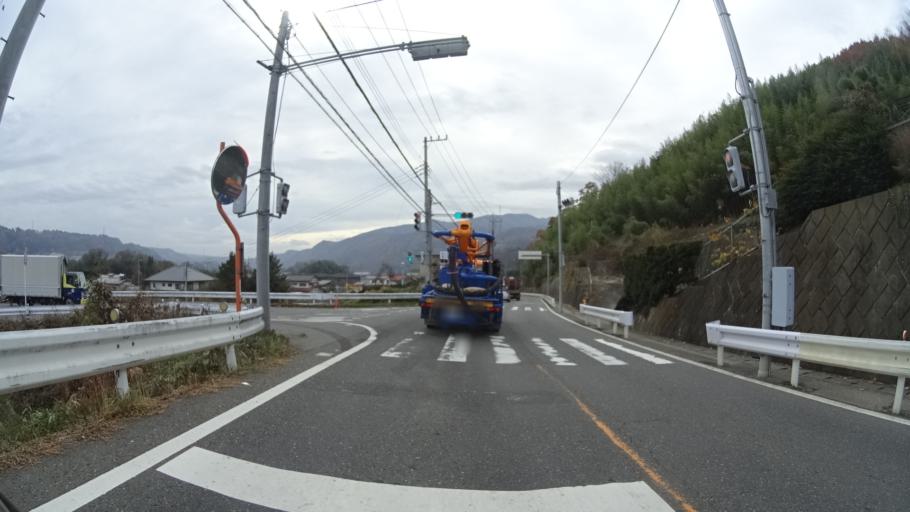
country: JP
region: Gunma
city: Numata
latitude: 36.6237
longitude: 139.0451
